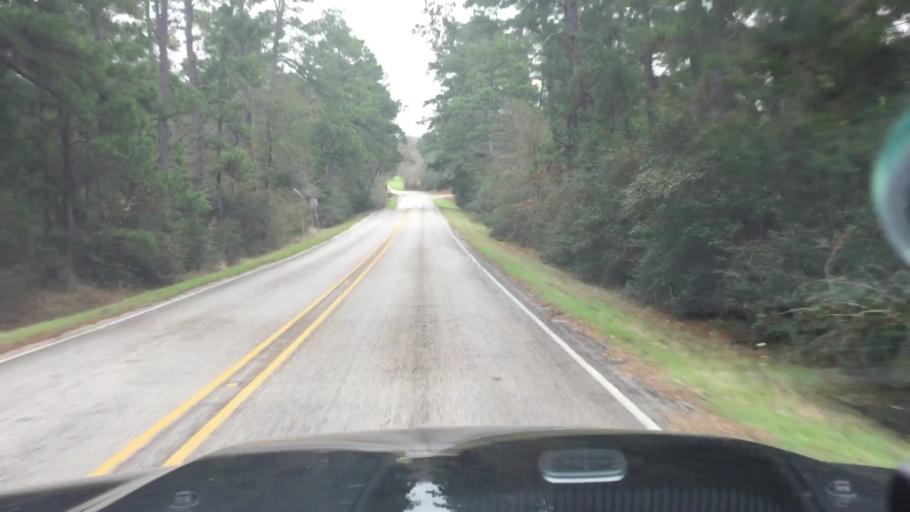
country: US
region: Texas
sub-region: Fayette County
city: La Grange
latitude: 30.0122
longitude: -96.9222
